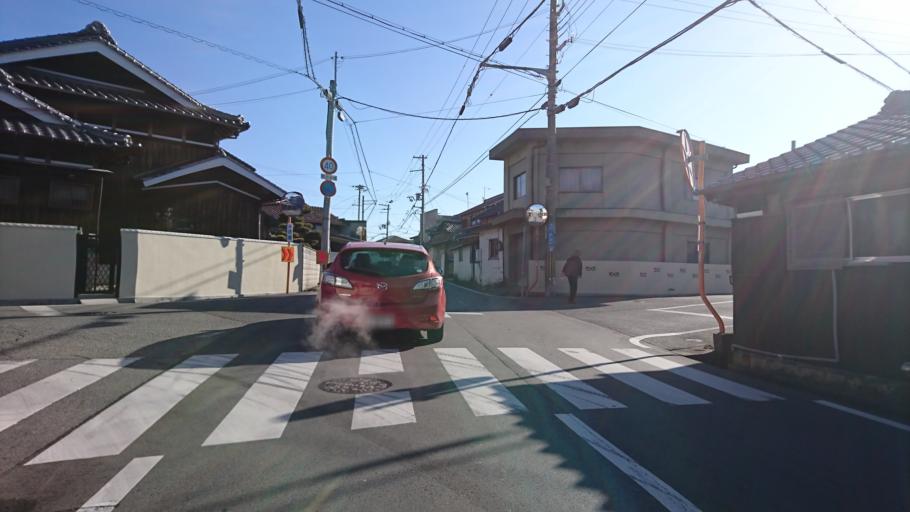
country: JP
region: Hyogo
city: Kakogawacho-honmachi
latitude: 34.7523
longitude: 134.8881
